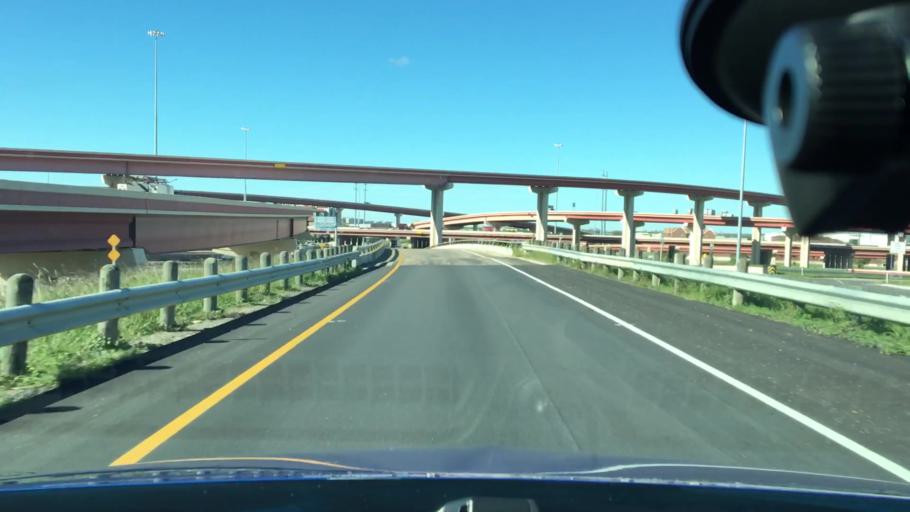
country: US
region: Texas
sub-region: Dallas County
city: Irving
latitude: 32.8377
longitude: -97.0131
